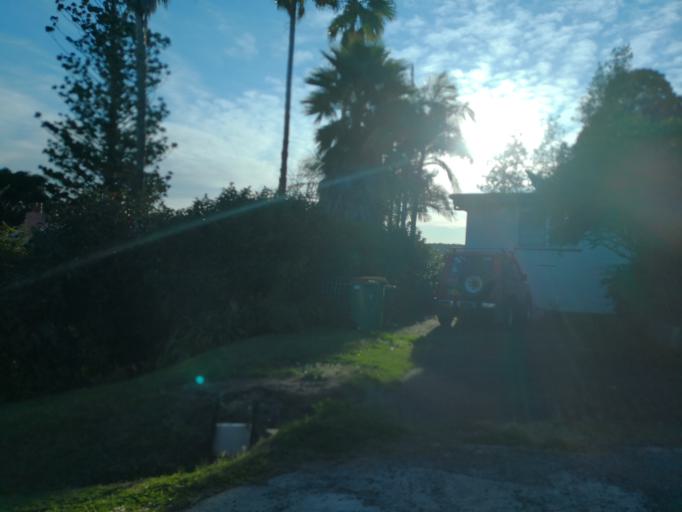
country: AU
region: New South Wales
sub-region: Gosford Shire
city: Narara
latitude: -33.4017
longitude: 151.3504
